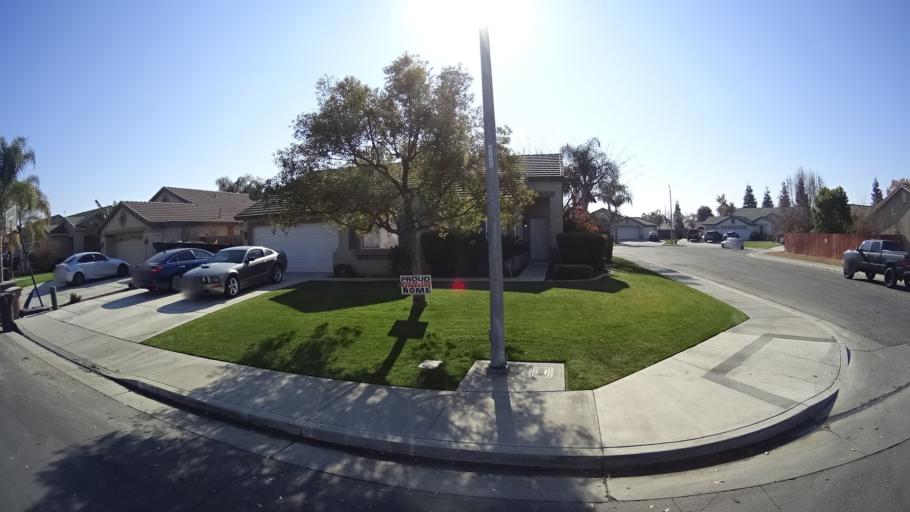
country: US
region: California
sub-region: Kern County
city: Greenacres
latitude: 35.3140
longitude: -119.1134
